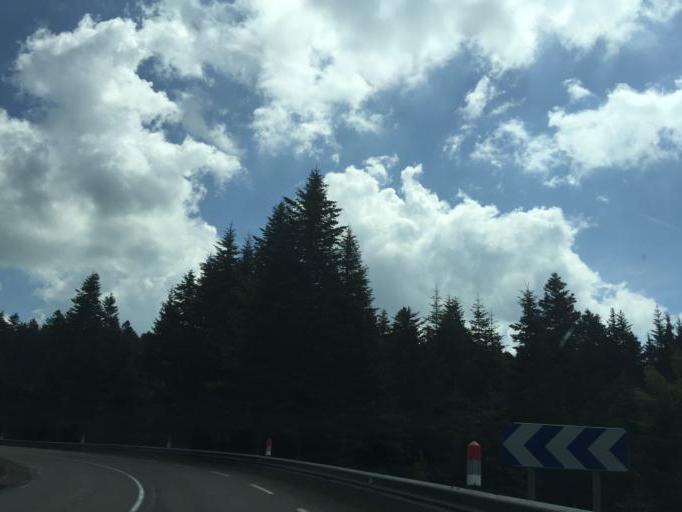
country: FR
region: Rhone-Alpes
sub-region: Departement de la Loire
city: Saint-Genest-Malifaux
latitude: 45.3464
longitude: 4.4817
